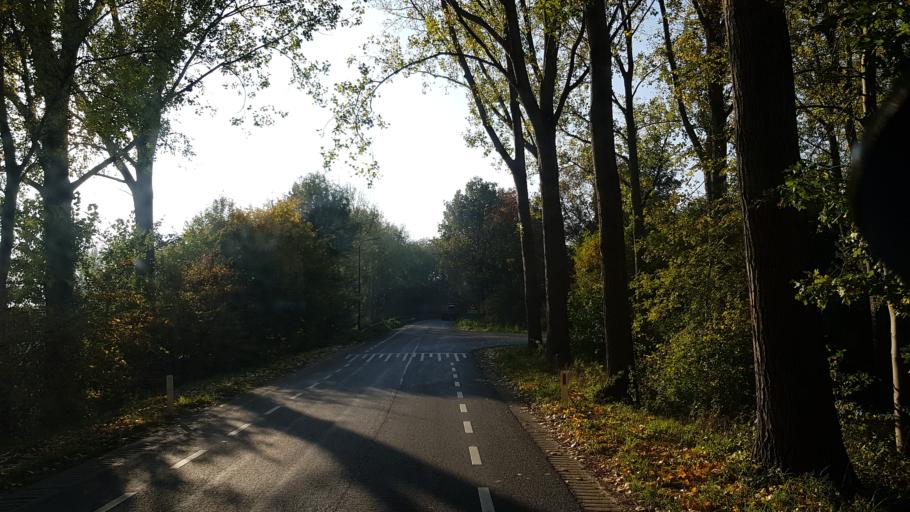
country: NL
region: Gelderland
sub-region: Gemeente Apeldoorn
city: Loenen
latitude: 52.1744
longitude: 6.0317
